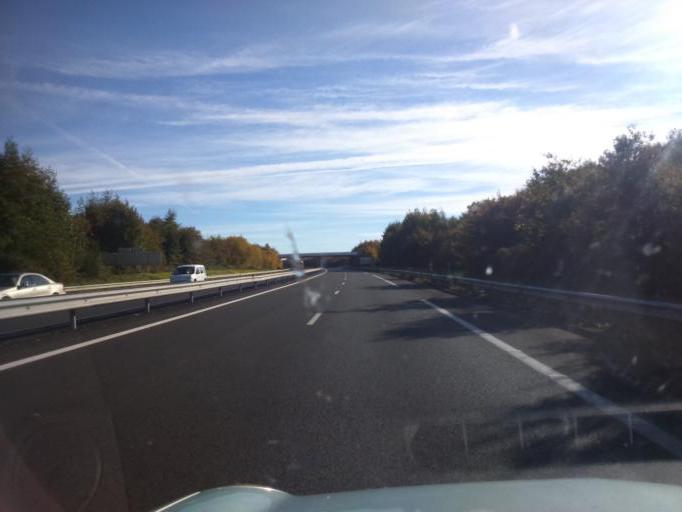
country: FR
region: Poitou-Charentes
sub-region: Departement de la Charente-Maritime
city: Tonnay-Charente
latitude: 45.9547
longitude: -0.9024
